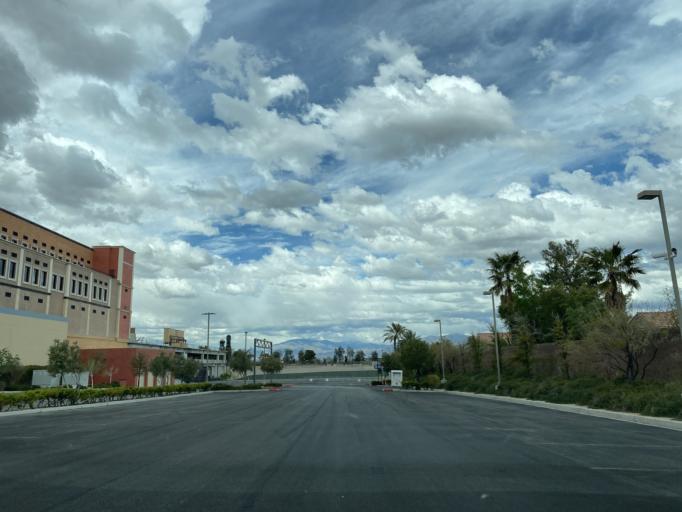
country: US
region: Nevada
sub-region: Clark County
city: Summerlin South
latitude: 36.1676
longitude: -115.2848
